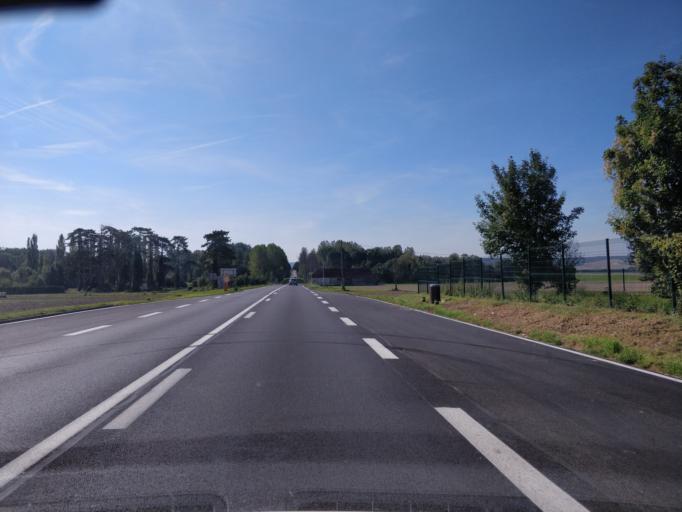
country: FR
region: Champagne-Ardenne
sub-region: Departement de l'Aube
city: Saint-Germain
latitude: 48.2493
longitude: 4.0259
